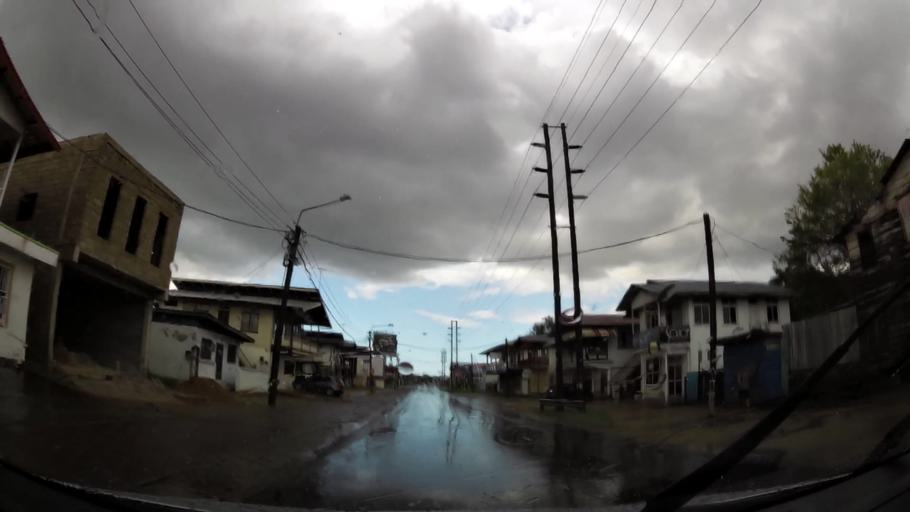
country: SR
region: Paramaribo
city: Paramaribo
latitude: 5.8274
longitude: -55.1697
